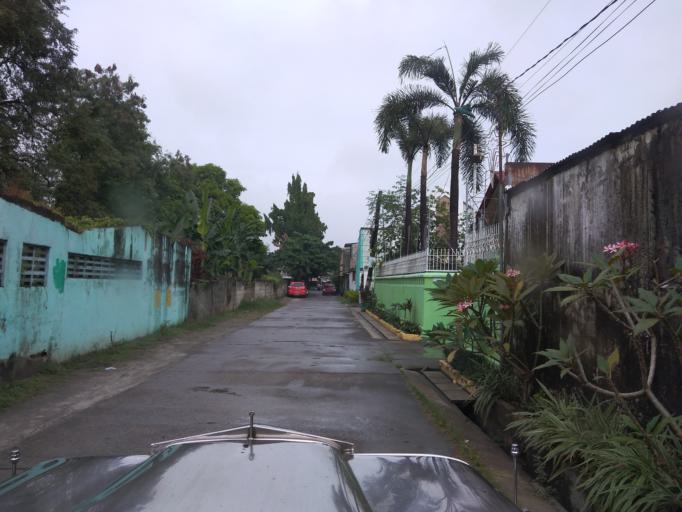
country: PH
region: Central Luzon
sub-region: Province of Pampanga
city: Mexico
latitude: 15.0650
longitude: 120.7226
